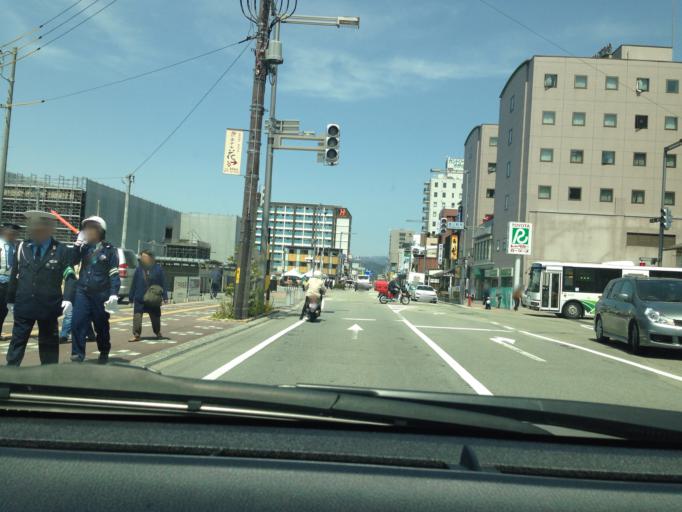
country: JP
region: Gifu
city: Takayama
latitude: 36.1402
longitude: 137.2521
